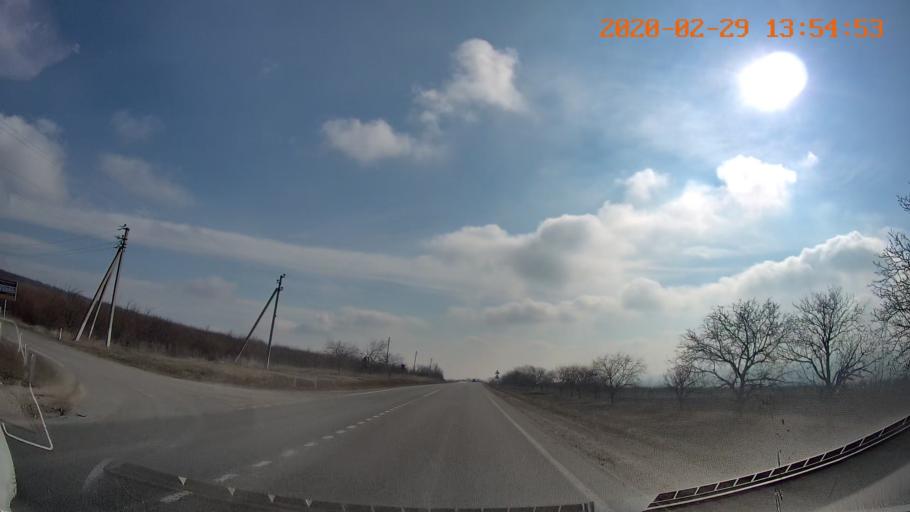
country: MD
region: Floresti
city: Leninskiy
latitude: 47.8266
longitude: 28.4306
